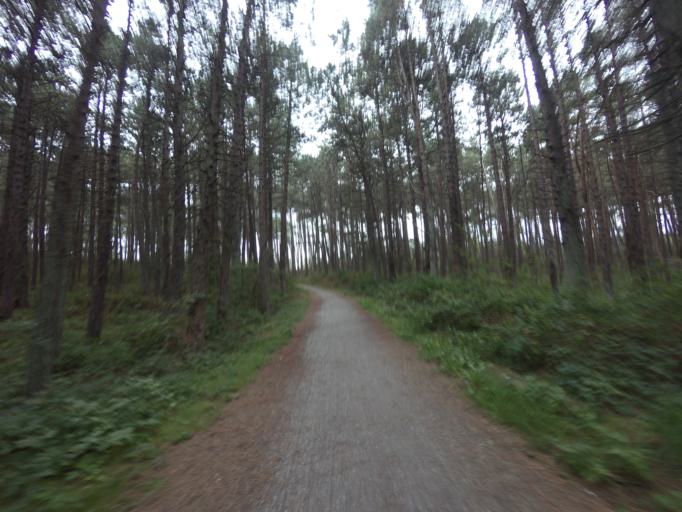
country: NL
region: Friesland
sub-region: Gemeente Schiermonnikoog
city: Schiermonnikoog
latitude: 53.4935
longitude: 6.1682
